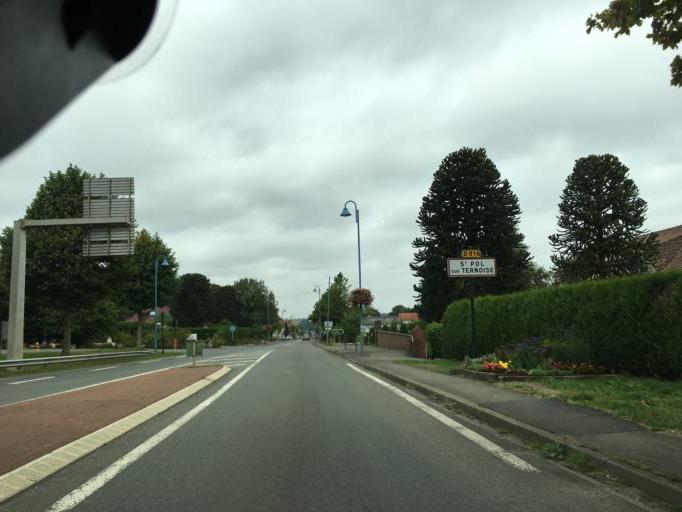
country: FR
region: Nord-Pas-de-Calais
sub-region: Departement du Pas-de-Calais
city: Saint-Pol-sur-Ternoise
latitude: 50.3683
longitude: 2.3314
